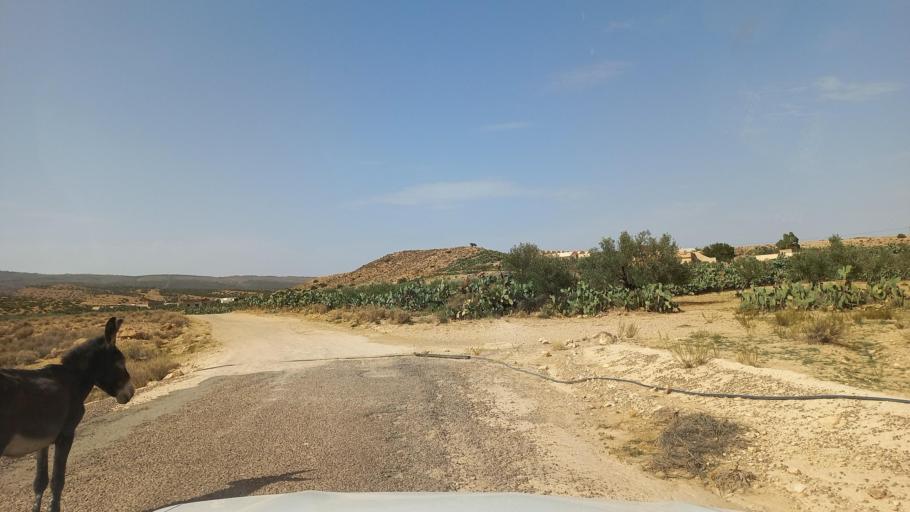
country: TN
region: Al Qasrayn
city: Kasserine
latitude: 35.3047
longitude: 8.9415
